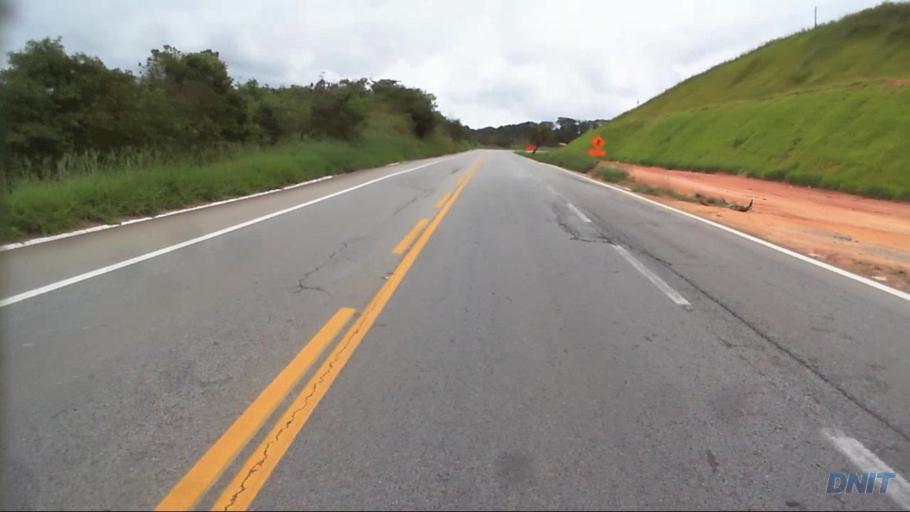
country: BR
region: Minas Gerais
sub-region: Barao De Cocais
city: Barao de Cocais
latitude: -19.7592
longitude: -43.4663
